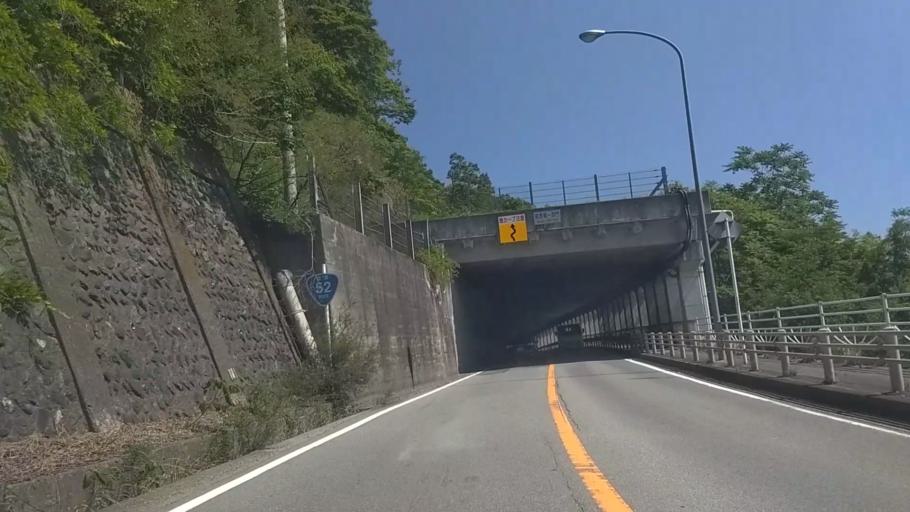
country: JP
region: Yamanashi
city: Ryuo
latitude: 35.5005
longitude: 138.4460
